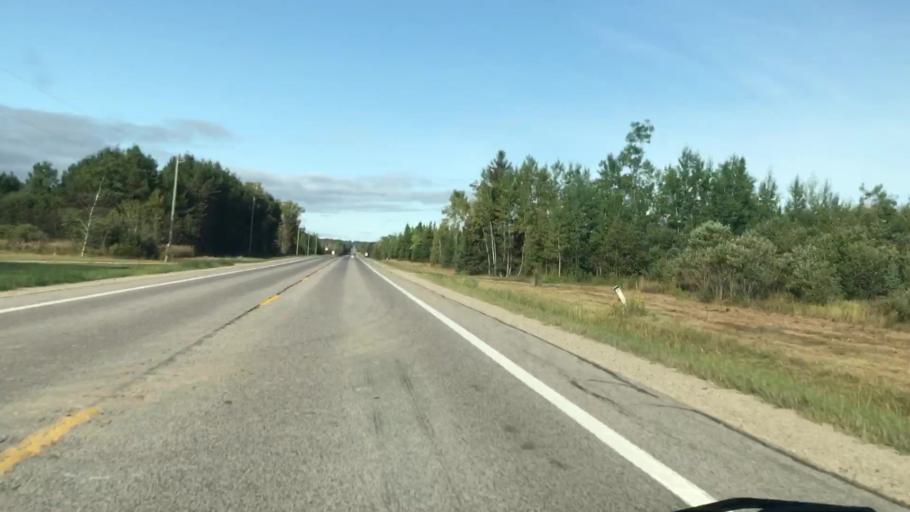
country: US
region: Michigan
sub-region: Luce County
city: Newberry
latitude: 46.3036
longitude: -85.3732
